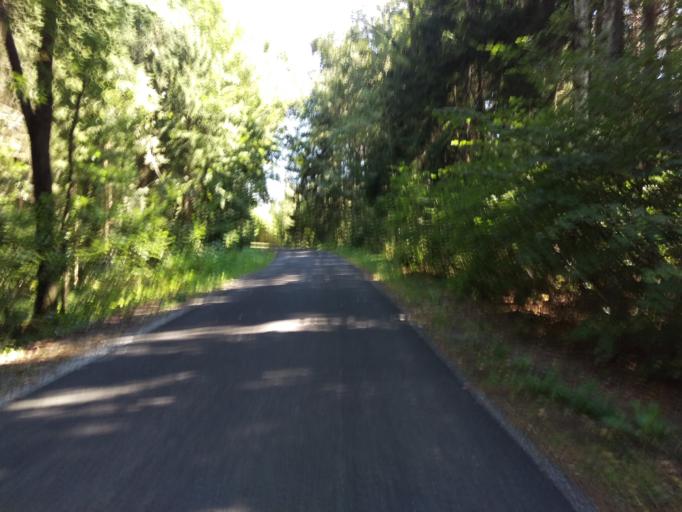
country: AT
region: Styria
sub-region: Politischer Bezirk Graz-Umgebung
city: Hart bei Graz
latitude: 47.0578
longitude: 15.5568
